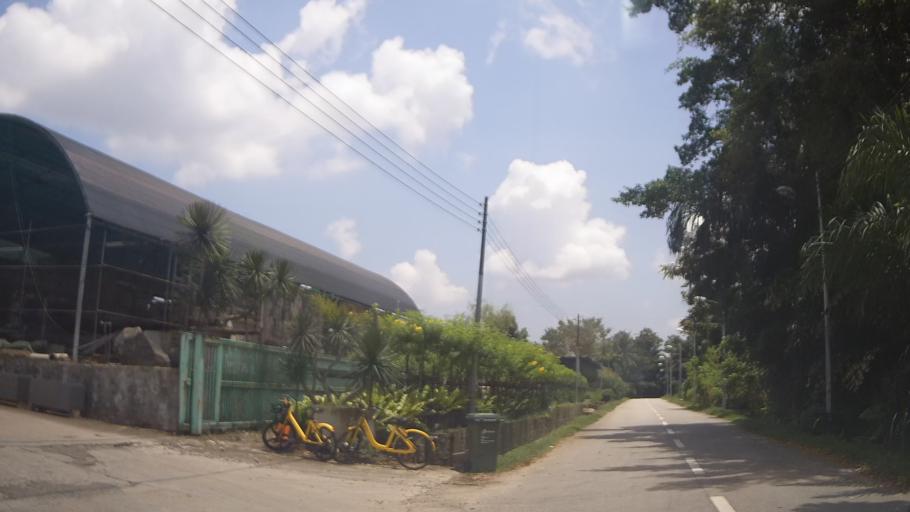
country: MY
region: Johor
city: Kampung Pasir Gudang Baru
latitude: 1.3983
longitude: 103.8649
